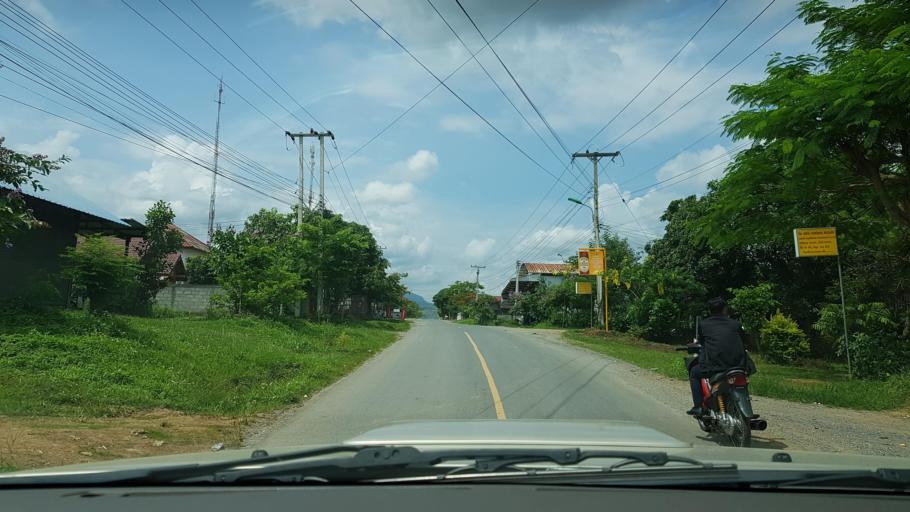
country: LA
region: Loungnamtha
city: Muang Nale
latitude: 20.1396
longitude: 101.4539
